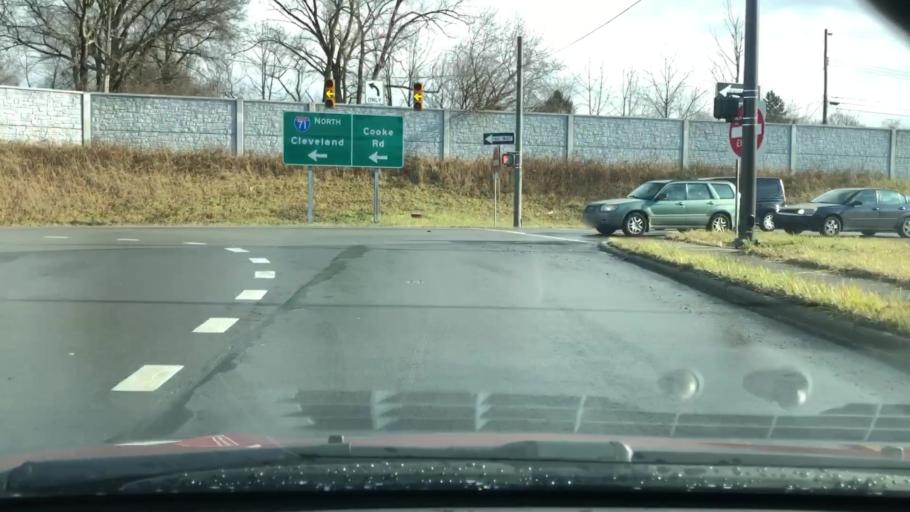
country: US
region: Ohio
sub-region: Franklin County
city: Worthington
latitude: 40.0464
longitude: -82.9968
